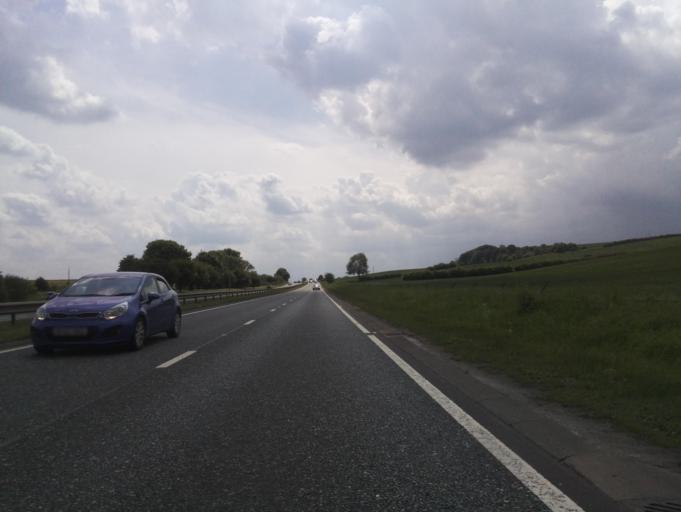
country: GB
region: England
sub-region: North Yorkshire
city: Northallerton
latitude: 54.3314
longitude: -1.3365
